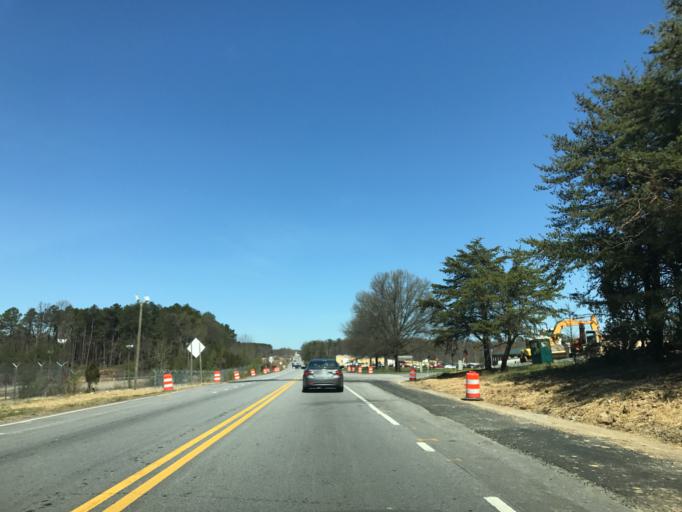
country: US
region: Maryland
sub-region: Anne Arundel County
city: Fort Meade
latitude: 39.1168
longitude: -76.7290
